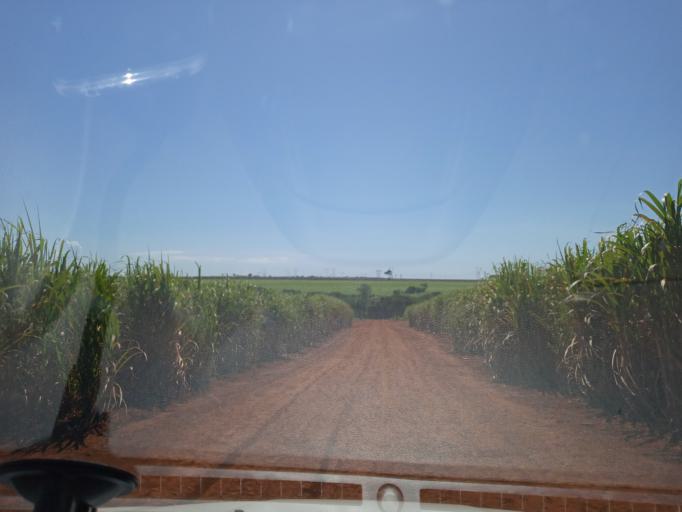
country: BR
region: Goias
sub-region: Itumbiara
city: Itumbiara
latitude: -18.4416
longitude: -49.1467
